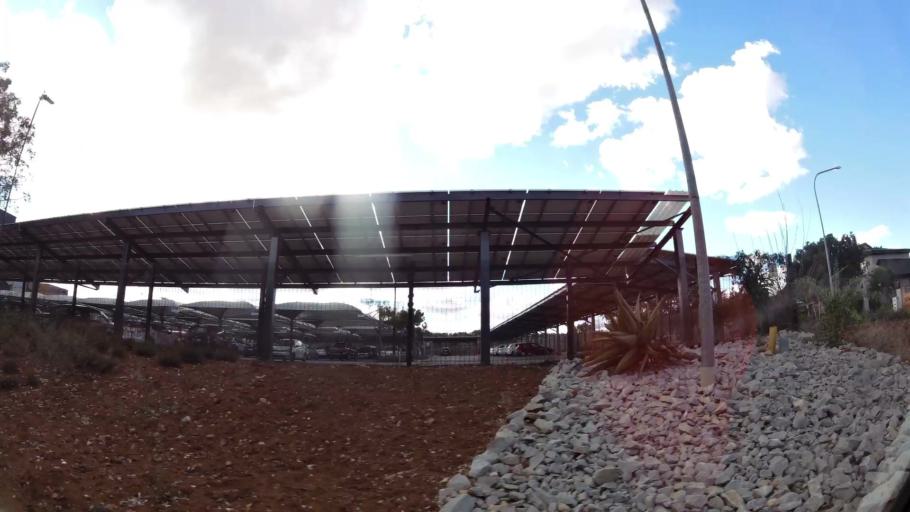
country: ZA
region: Limpopo
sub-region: Capricorn District Municipality
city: Polokwane
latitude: -23.9022
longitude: 29.4949
